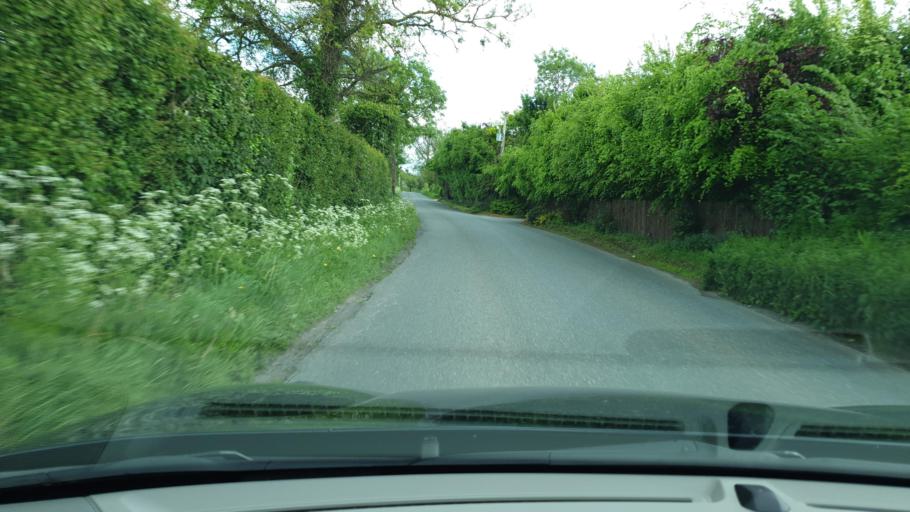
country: IE
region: Leinster
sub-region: An Mhi
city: Ashbourne
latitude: 53.5319
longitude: -6.4264
